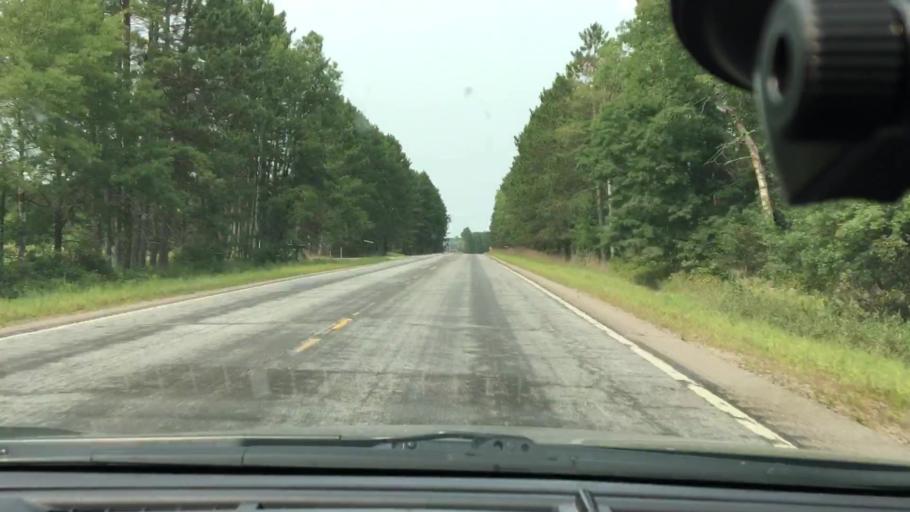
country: US
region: Minnesota
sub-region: Crow Wing County
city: Cross Lake
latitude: 46.7494
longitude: -93.9670
